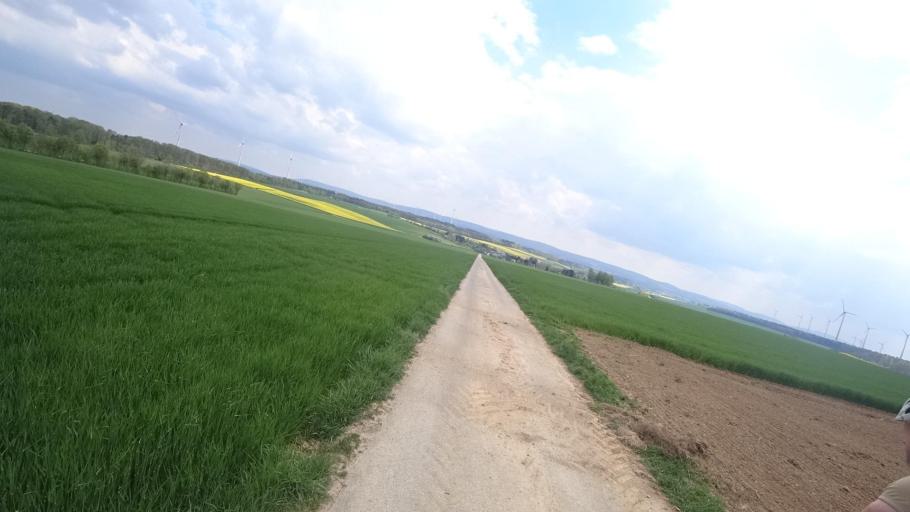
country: DE
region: Rheinland-Pfalz
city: Klosterkumbd
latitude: 50.0358
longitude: 7.5296
